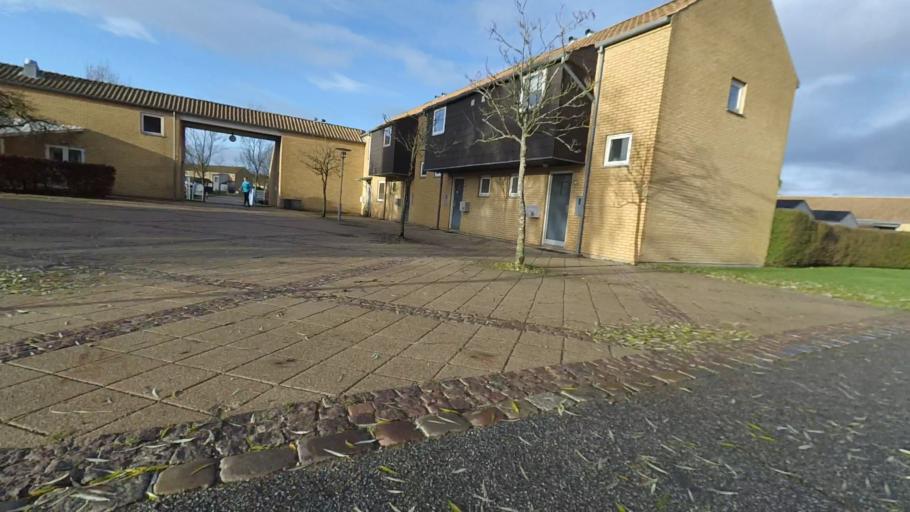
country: DK
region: Central Jutland
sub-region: Arhus Kommune
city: Marslet
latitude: 56.1040
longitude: 10.1716
